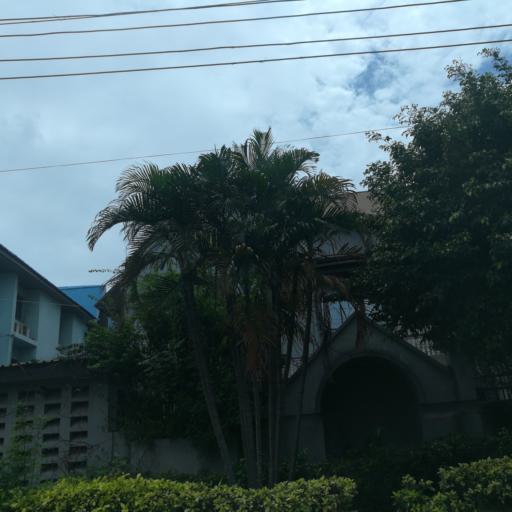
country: NG
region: Lagos
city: Ikoyi
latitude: 6.4447
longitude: 3.4597
